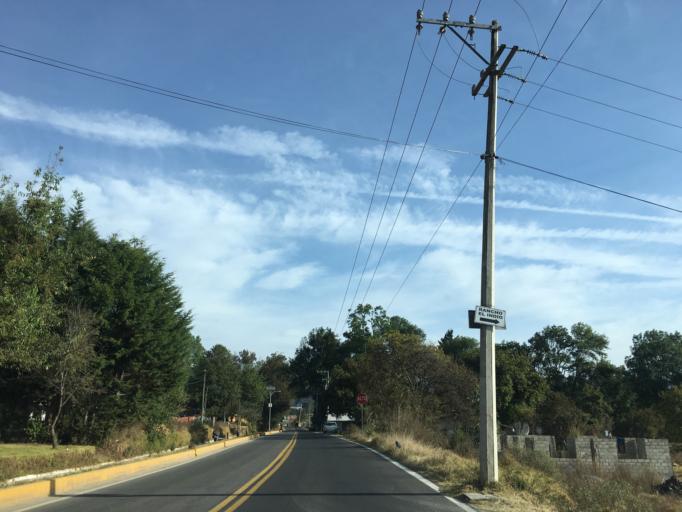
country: MX
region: Mexico
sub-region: Valle de Bravo
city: Colonia Rincon Villa del Valle
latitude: 19.1876
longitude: -100.1014
